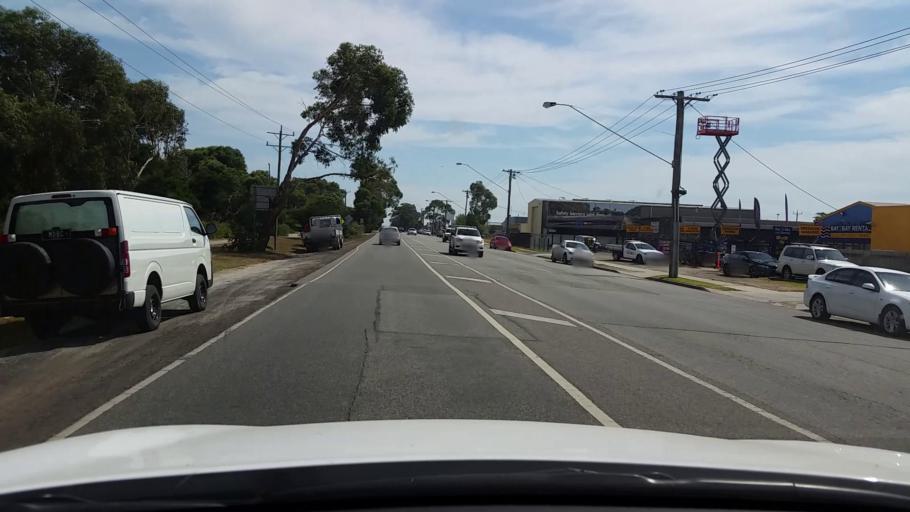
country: AU
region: Victoria
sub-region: Mornington Peninsula
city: Hastings
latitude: -38.3059
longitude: 145.1836
